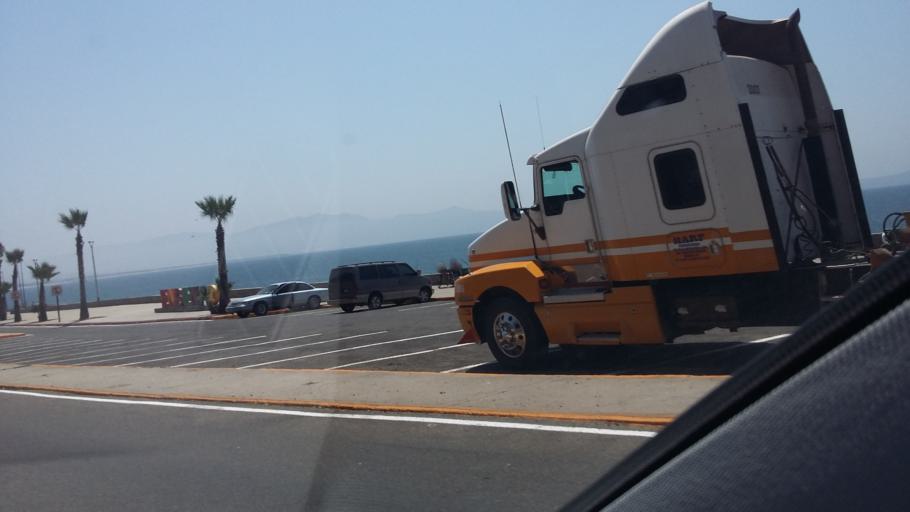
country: MX
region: Baja California
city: Ensenada
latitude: 31.8603
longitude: -116.6390
